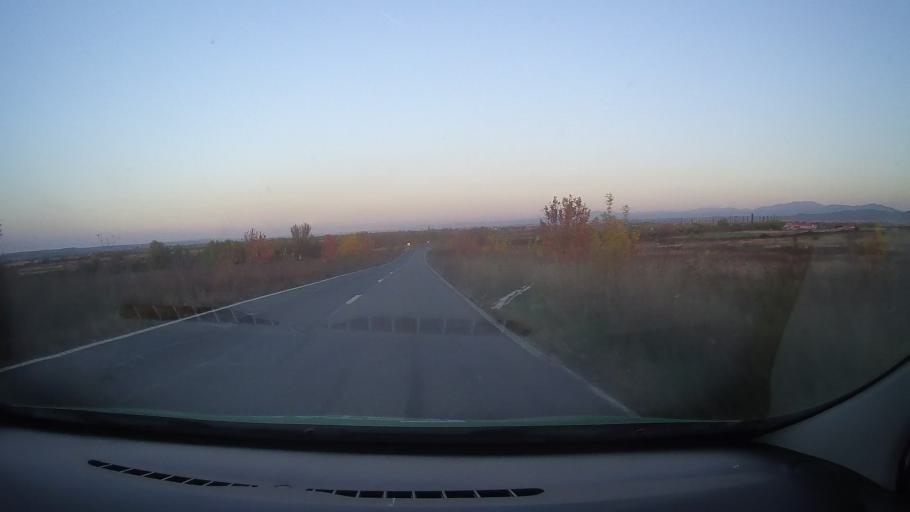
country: RO
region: Timis
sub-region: Comuna Dumbrava
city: Rachita
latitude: 45.8246
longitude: 22.0902
